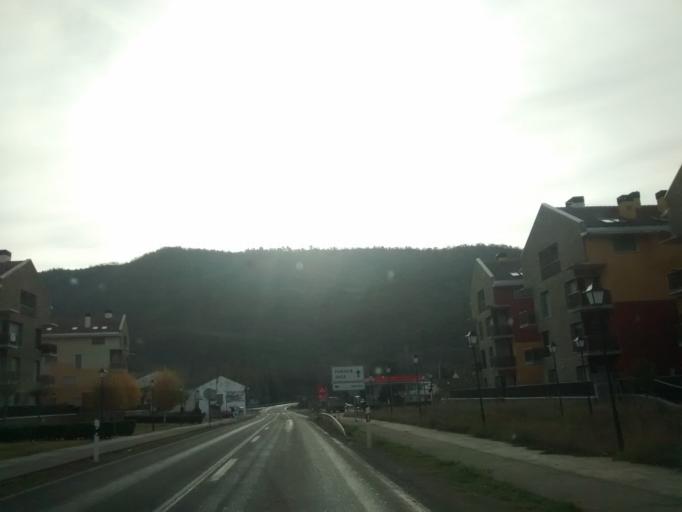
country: ES
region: Aragon
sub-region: Provincia de Huesca
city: Bailo
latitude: 42.5578
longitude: -0.7869
